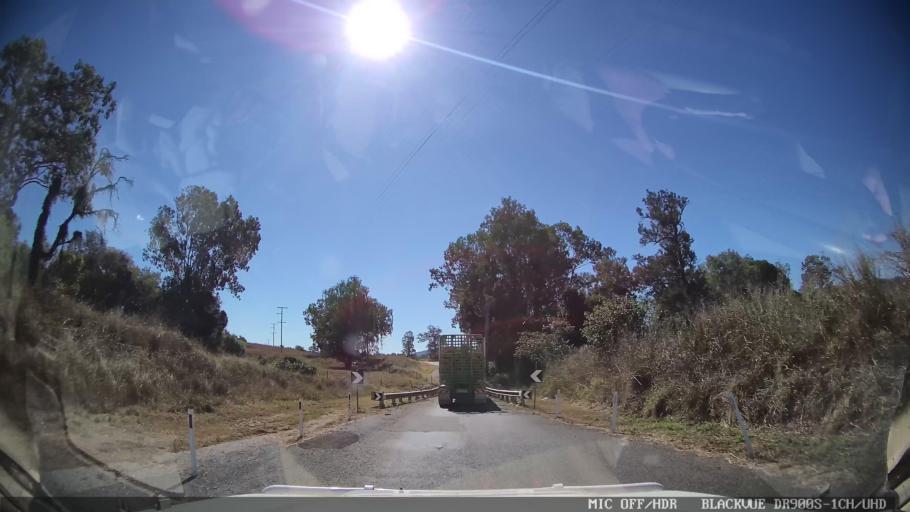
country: AU
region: Queensland
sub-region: Gladstone
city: Toolooa
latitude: -24.2746
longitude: 151.2761
